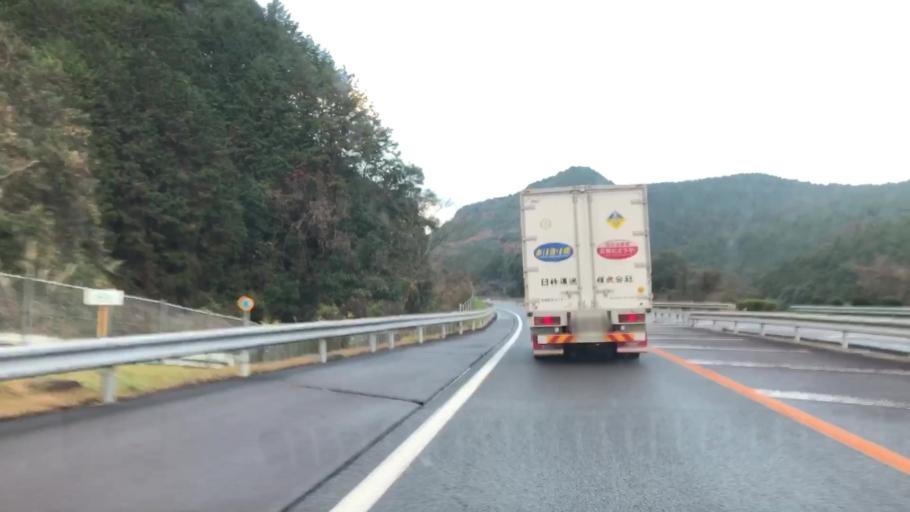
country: JP
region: Saga Prefecture
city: Ureshinomachi-shimojuku
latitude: 33.1559
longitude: 129.9236
